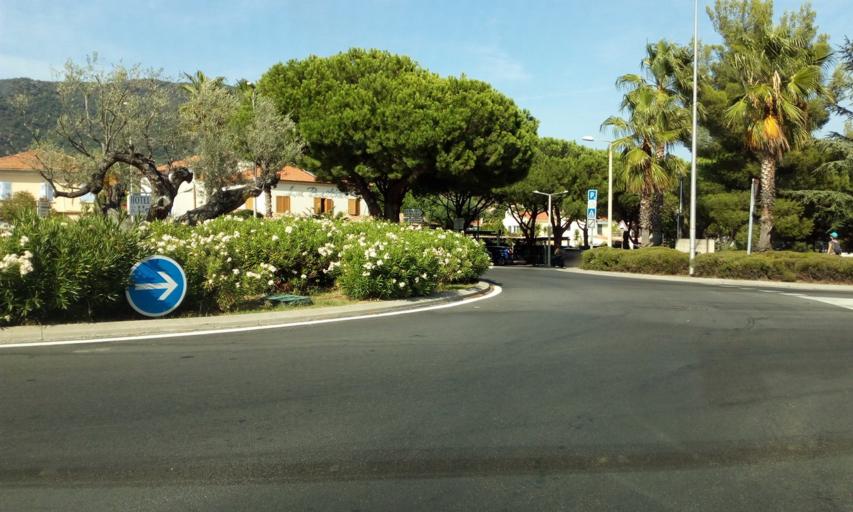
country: FR
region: Provence-Alpes-Cote d'Azur
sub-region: Departement du Var
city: Le Lavandou
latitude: 43.1409
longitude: 6.3796
